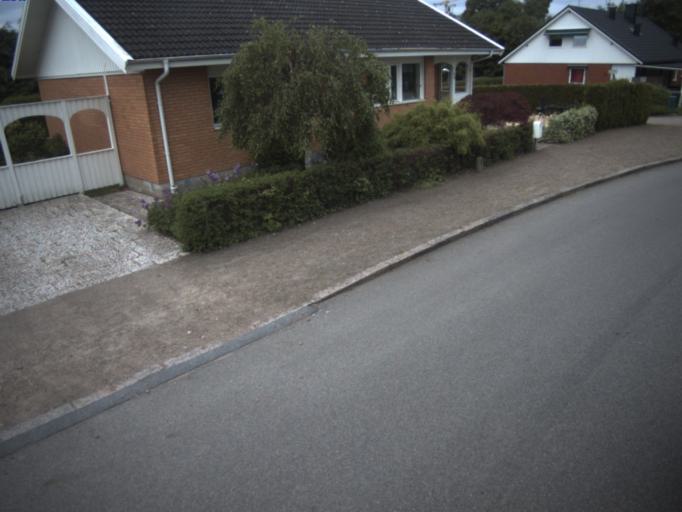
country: SE
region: Skane
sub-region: Helsingborg
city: Helsingborg
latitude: 56.0328
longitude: 12.7297
